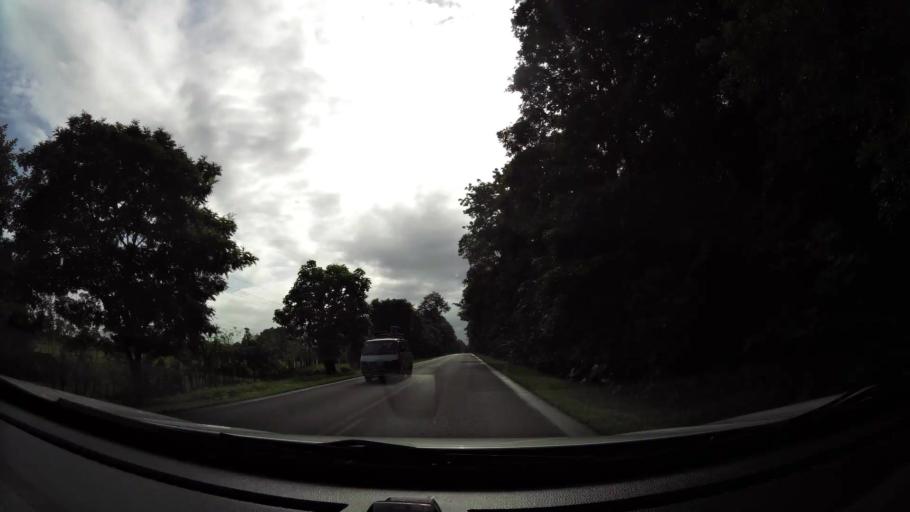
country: CR
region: Limon
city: Pocora
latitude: 10.1913
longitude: -83.6388
